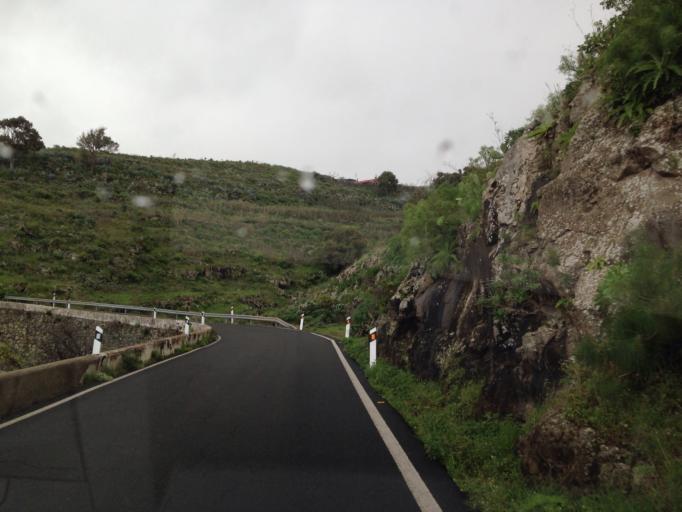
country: ES
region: Canary Islands
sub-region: Provincia de Las Palmas
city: Guia
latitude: 28.1157
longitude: -15.6442
